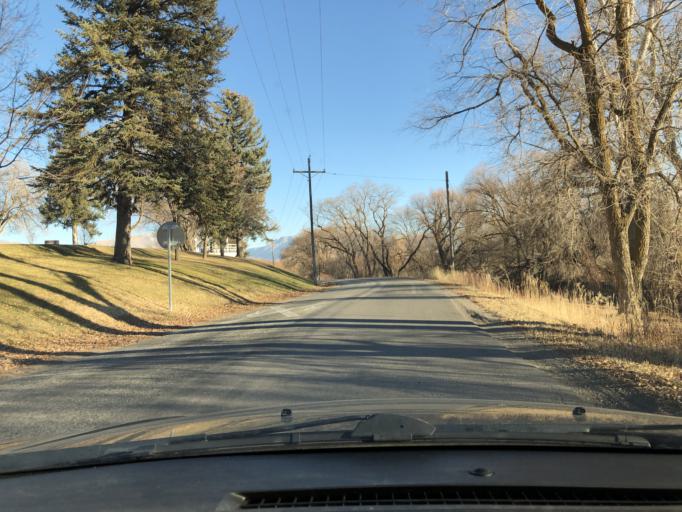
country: US
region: Utah
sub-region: Cache County
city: Wellsville
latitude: 41.6470
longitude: -111.9281
